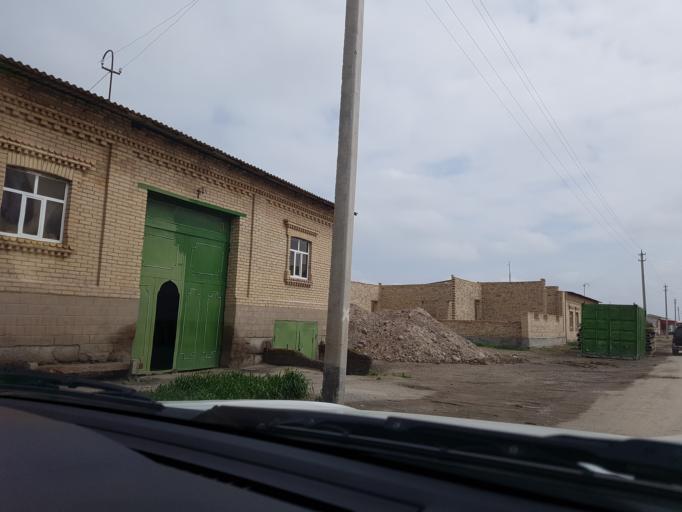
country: TM
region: Lebap
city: Turkmenabat
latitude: 38.9710
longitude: 63.6934
